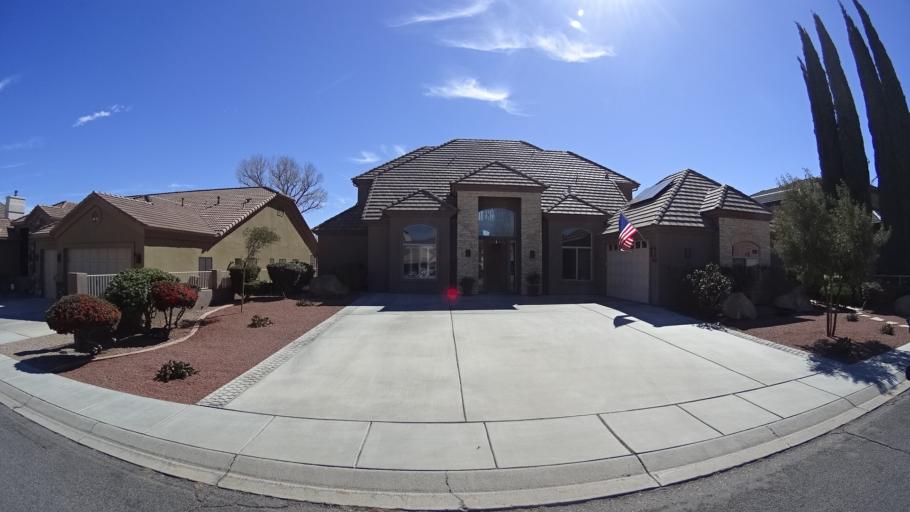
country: US
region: Arizona
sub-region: Mohave County
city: Kingman
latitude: 35.2115
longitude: -114.0509
